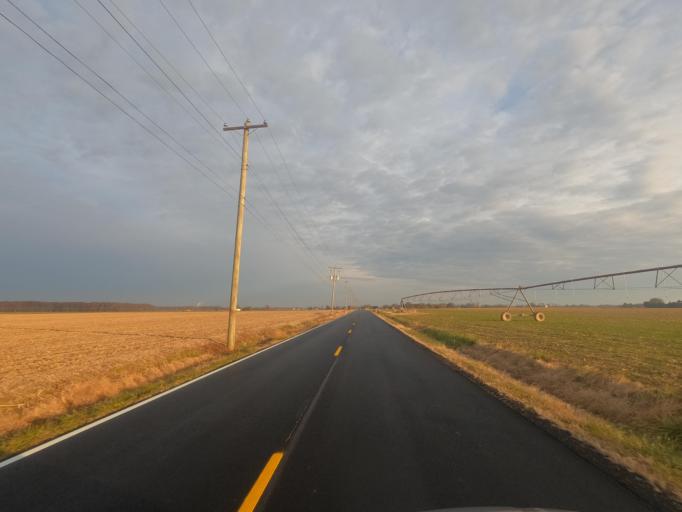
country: US
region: Delaware
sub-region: New Castle County
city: Townsend
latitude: 39.2975
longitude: -75.8305
